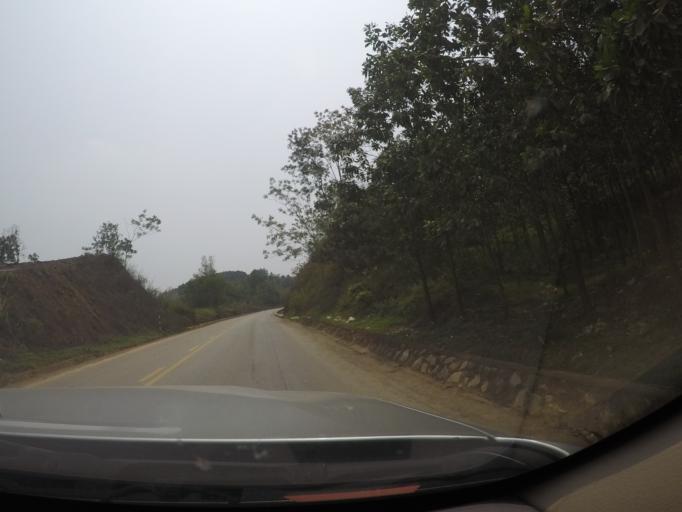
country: VN
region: Thanh Hoa
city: Thi Tran Thuong Xuan
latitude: 19.8654
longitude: 105.4118
